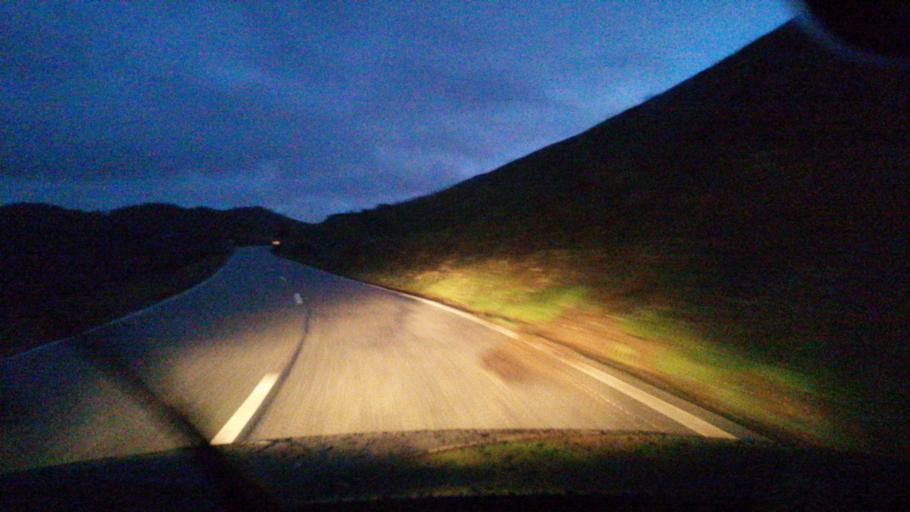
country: PT
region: Viseu
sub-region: Tabuaco
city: Tabuaco
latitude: 41.1466
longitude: -7.5426
